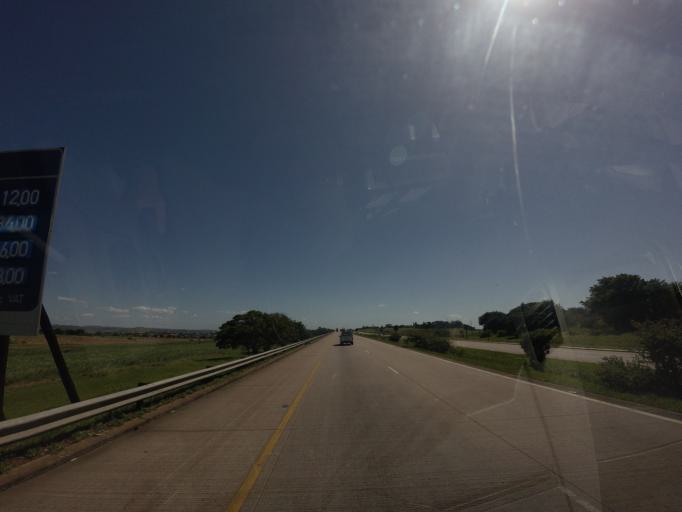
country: ZA
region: KwaZulu-Natal
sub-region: iLembe District Municipality
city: Stanger
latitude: -29.4142
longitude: 31.2781
